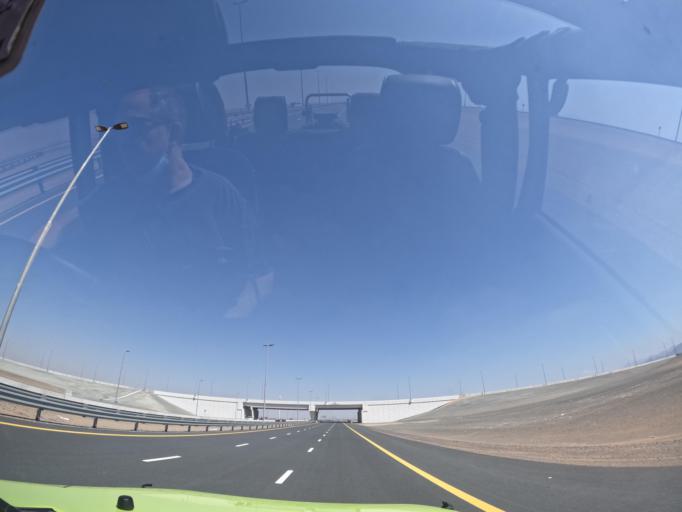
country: AE
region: Ash Shariqah
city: Adh Dhayd
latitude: 25.0709
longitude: 55.9088
